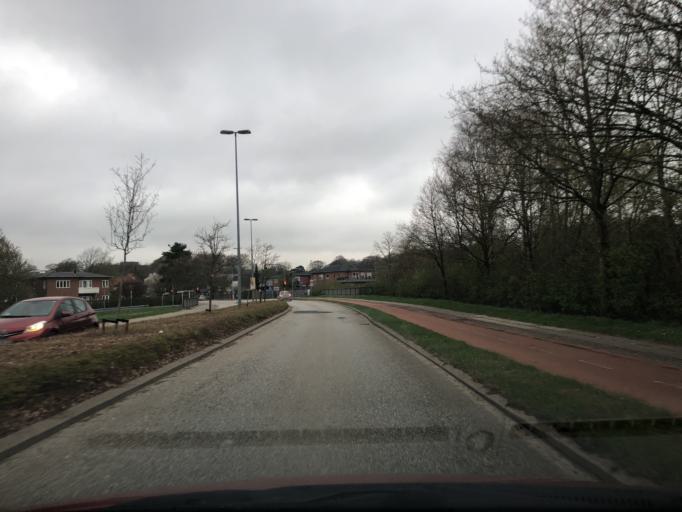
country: DK
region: Central Jutland
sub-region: Holstebro Kommune
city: Holstebro
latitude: 56.3553
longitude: 8.6224
